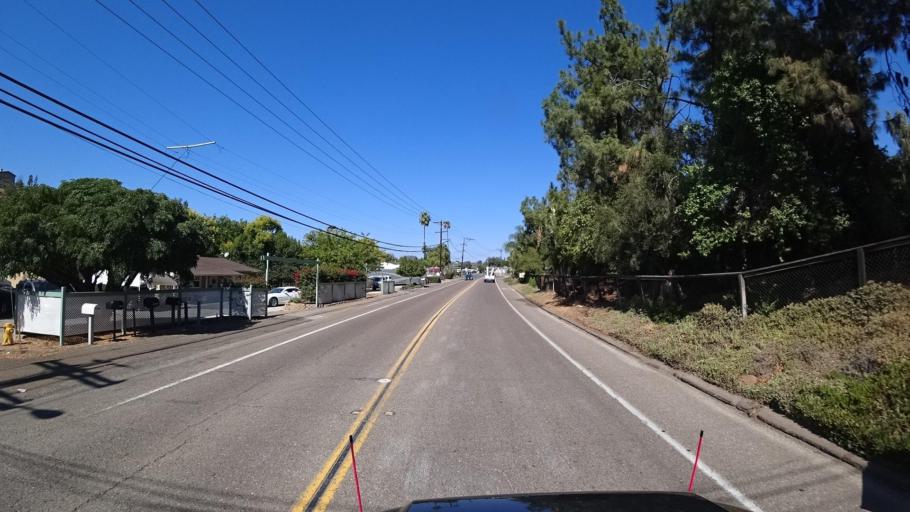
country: US
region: California
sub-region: San Diego County
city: Granite Hills
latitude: 32.8095
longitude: -116.9135
